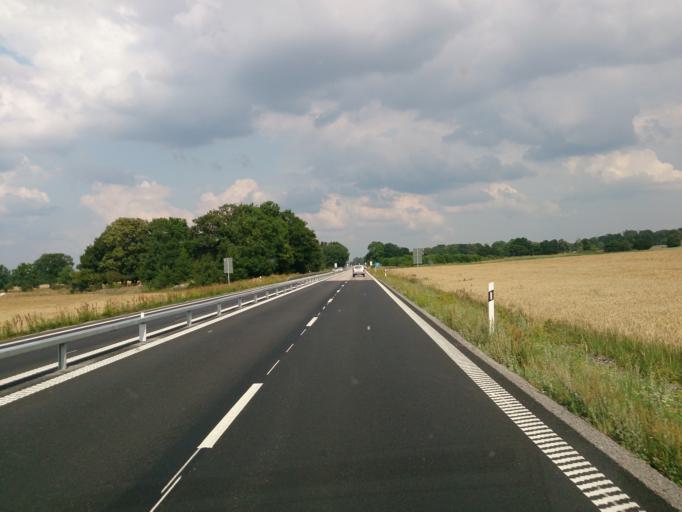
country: SE
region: Skane
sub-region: Hoors Kommun
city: Loberod
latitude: 55.8351
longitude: 13.5590
